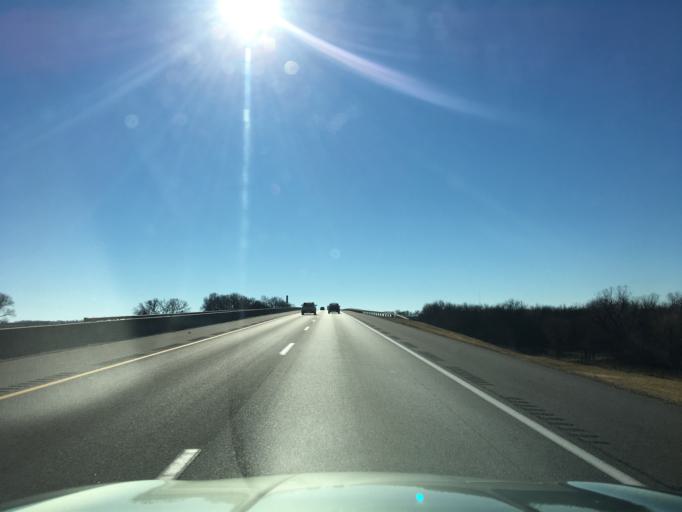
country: US
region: Kansas
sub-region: Sumner County
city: Belle Plaine
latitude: 37.3546
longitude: -97.3222
